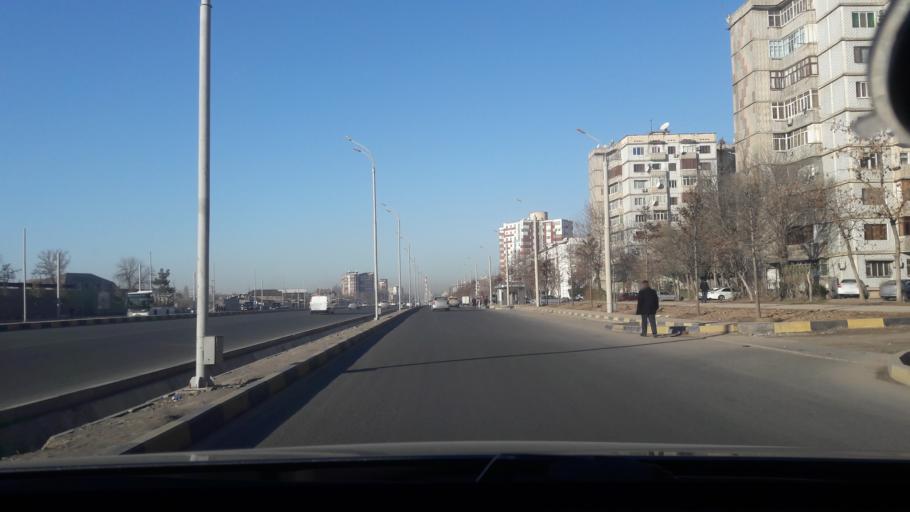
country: TJ
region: Dushanbe
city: Dushanbe
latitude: 38.5586
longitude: 68.7600
